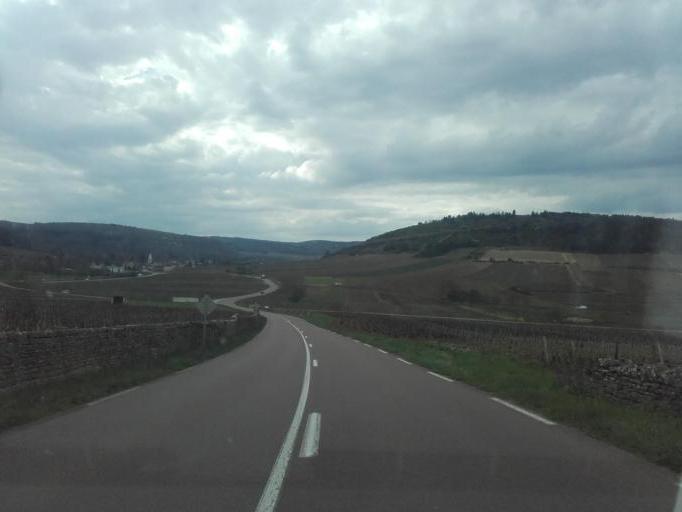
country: FR
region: Bourgogne
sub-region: Departement de la Cote-d'Or
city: Meursault
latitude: 46.9888
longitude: 4.7659
